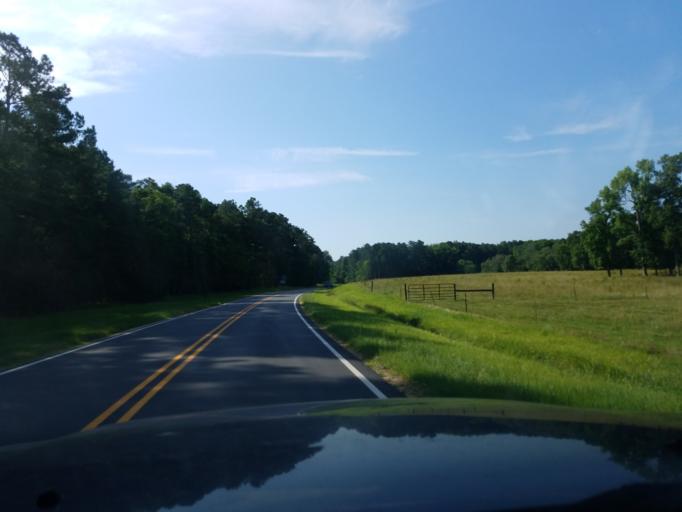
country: US
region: North Carolina
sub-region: Granville County
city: Butner
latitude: 36.1755
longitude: -78.7954
